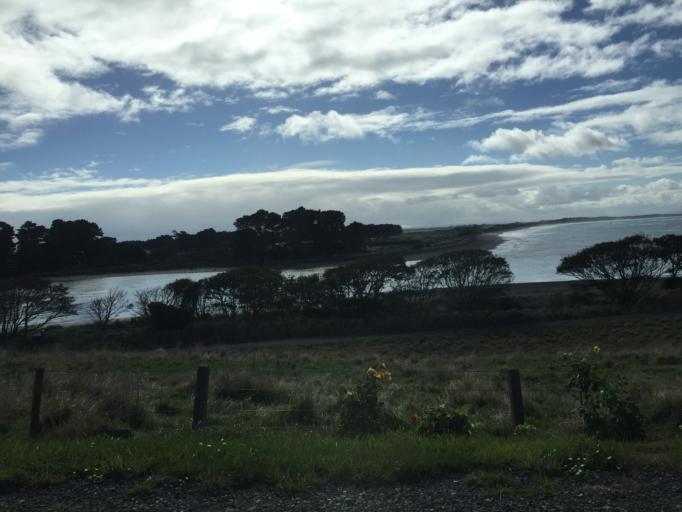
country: NZ
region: Southland
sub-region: Southland District
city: Riverton
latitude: -46.3599
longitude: 168.0200
